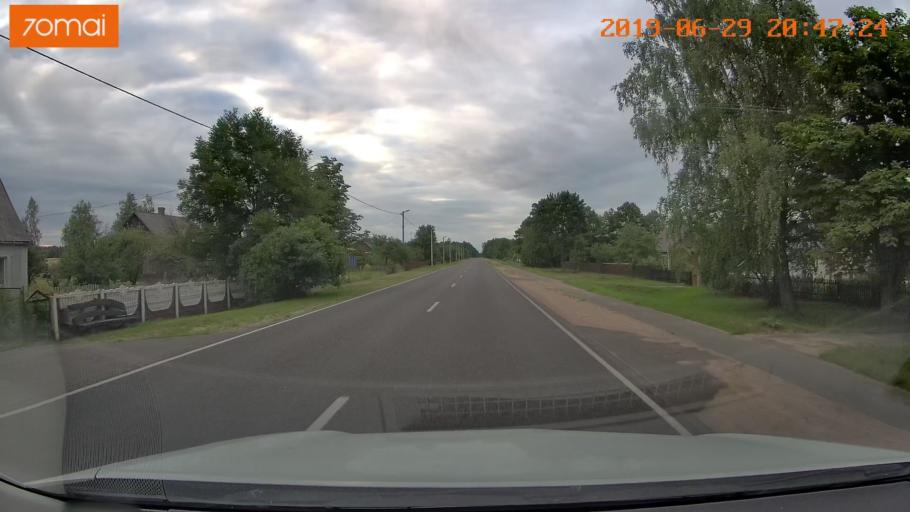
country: BY
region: Brest
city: Hantsavichy
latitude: 52.6381
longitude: 26.3153
